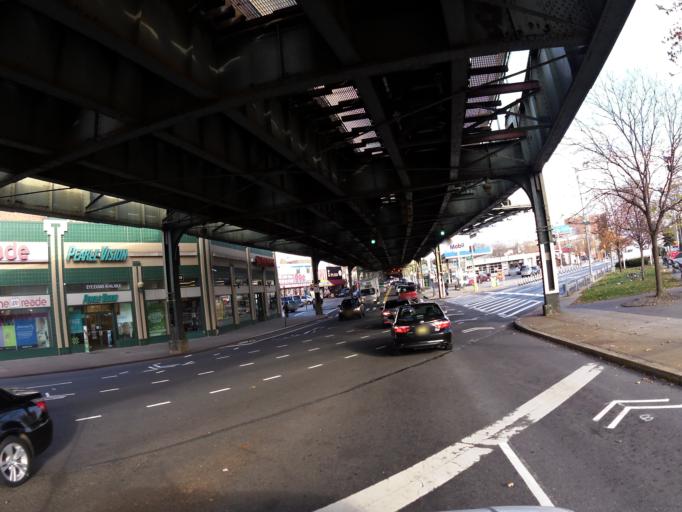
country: US
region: New York
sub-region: Queens County
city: Long Island City
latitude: 40.7429
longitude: -73.9164
